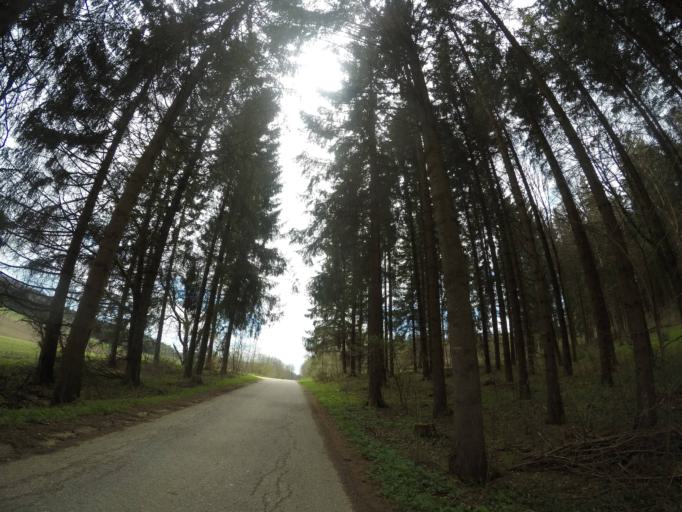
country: DE
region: Baden-Wuerttemberg
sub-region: Tuebingen Region
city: Laichingen
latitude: 48.4938
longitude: 9.6556
